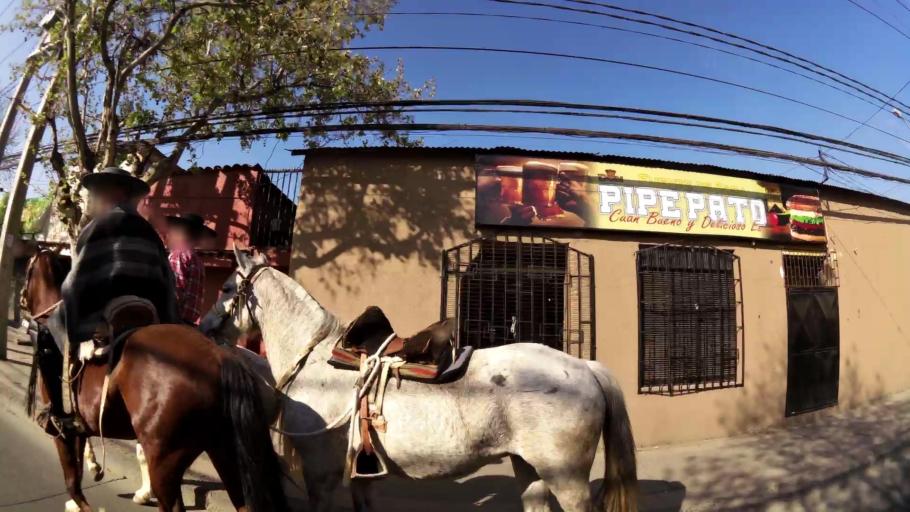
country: CL
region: Santiago Metropolitan
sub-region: Provincia de Santiago
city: Villa Presidente Frei, Nunoa, Santiago, Chile
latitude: -33.3610
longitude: -70.5056
